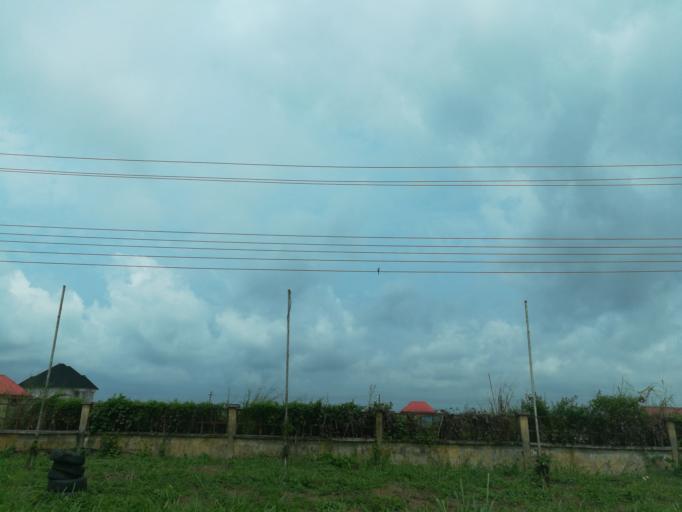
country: NG
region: Rivers
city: Port Harcourt
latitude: 4.8937
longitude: 6.9835
